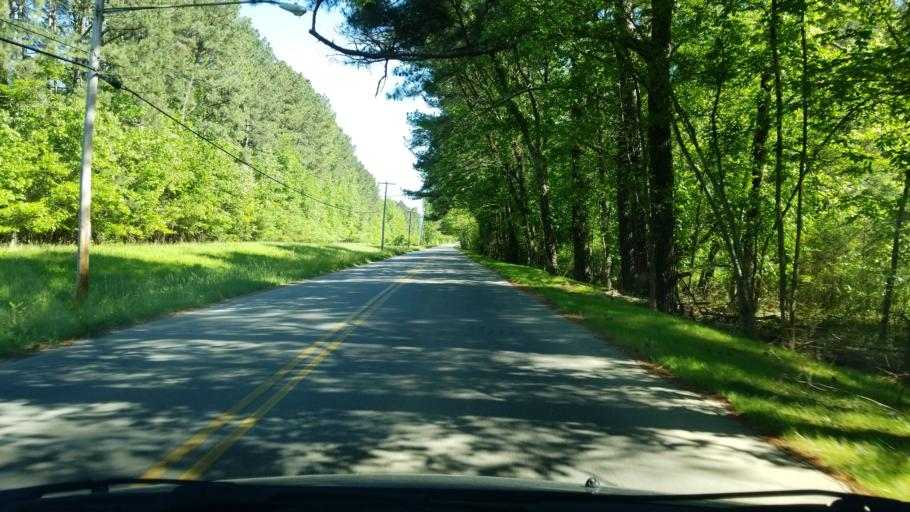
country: US
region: Tennessee
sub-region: Hamilton County
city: Chattanooga
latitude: 35.0372
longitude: -85.3346
